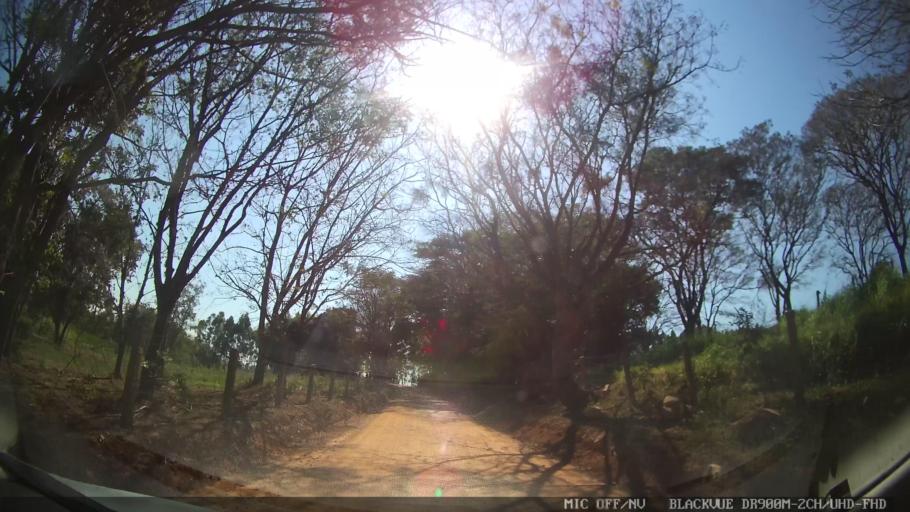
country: BR
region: Sao Paulo
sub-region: Itupeva
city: Itupeva
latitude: -23.0626
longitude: -47.0920
